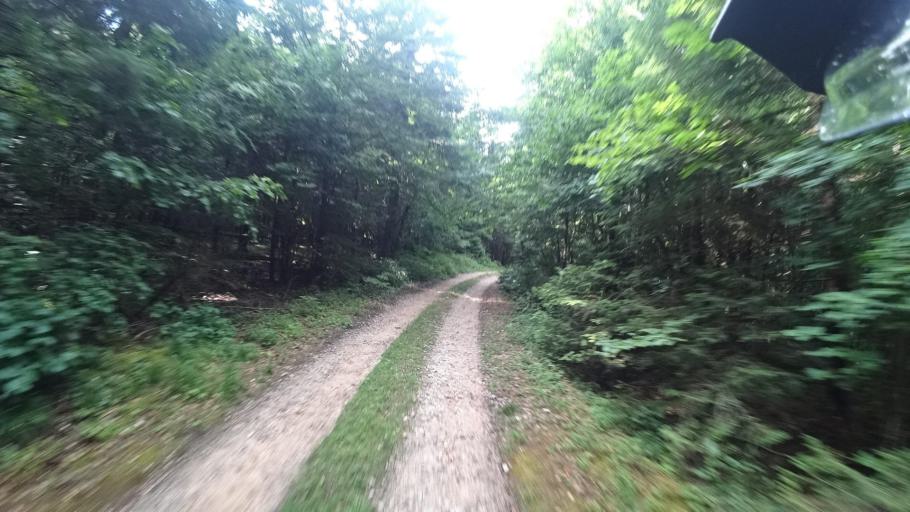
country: HR
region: Licko-Senjska
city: Jezerce
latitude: 44.7746
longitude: 15.6473
